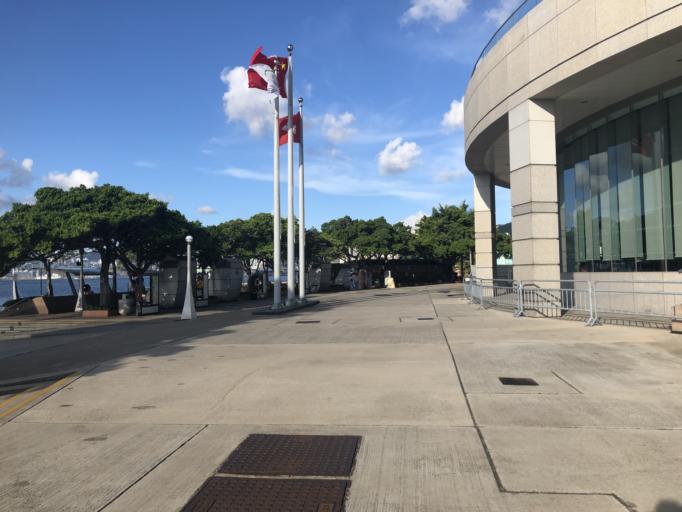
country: HK
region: Wanchai
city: Wan Chai
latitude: 22.2846
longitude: 114.1727
